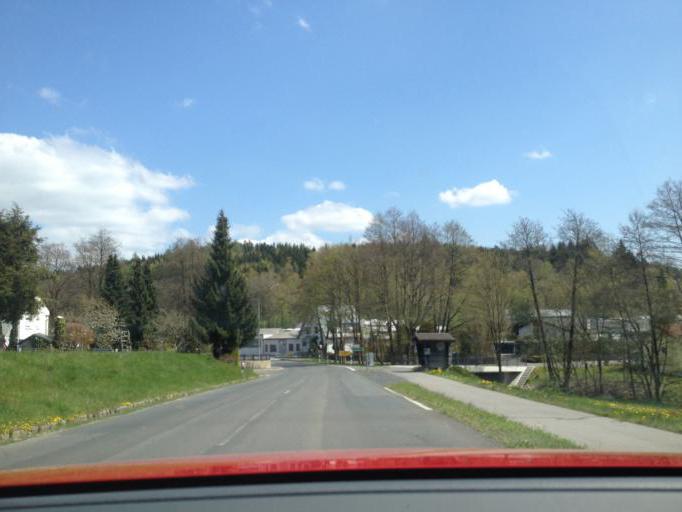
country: DE
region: Bavaria
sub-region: Upper Palatinate
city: Pullenreuth
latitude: 49.9333
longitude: 12.0015
